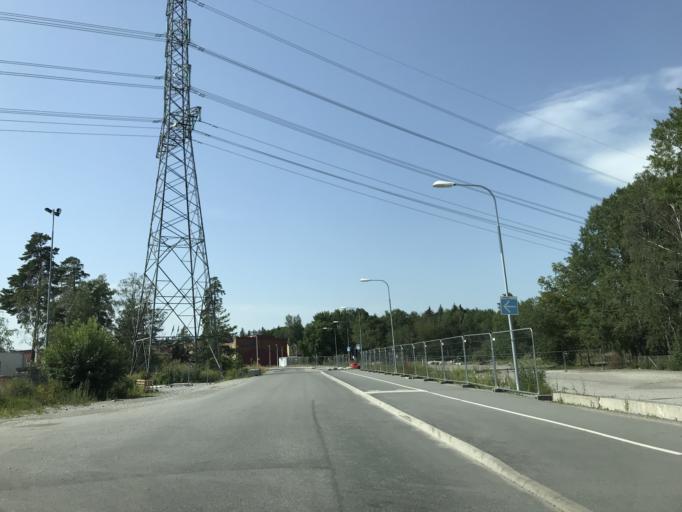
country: SE
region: Stockholm
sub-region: Solna Kommun
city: Rasunda
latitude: 59.3829
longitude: 17.9911
